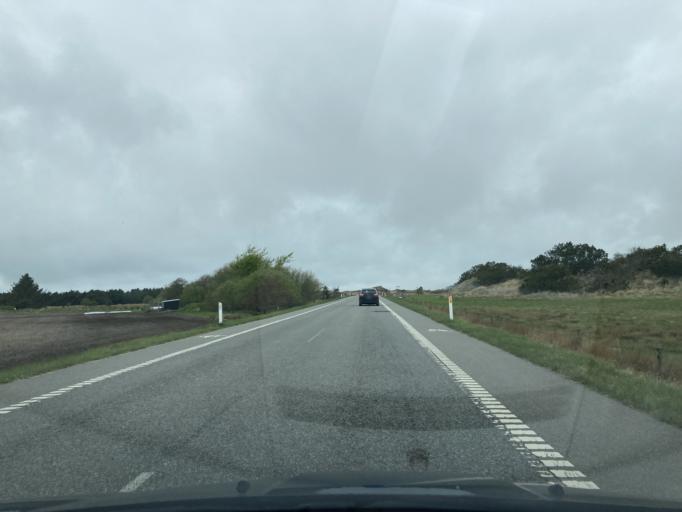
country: DK
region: North Denmark
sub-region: Thisted Kommune
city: Hurup
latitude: 56.9222
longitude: 8.3691
